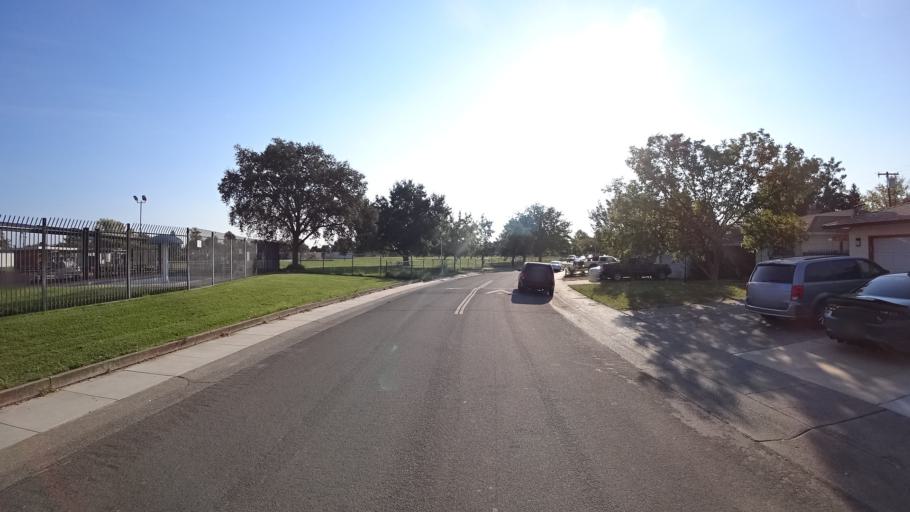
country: US
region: California
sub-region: Sacramento County
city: Parkway
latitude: 38.4915
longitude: -121.4989
